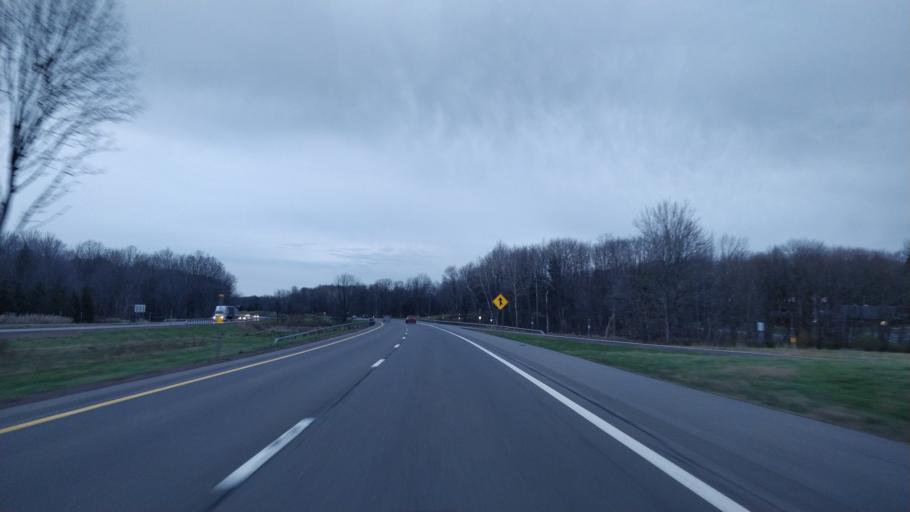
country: US
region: New York
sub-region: Oswego County
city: Central Square
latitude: 43.4063
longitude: -76.1161
